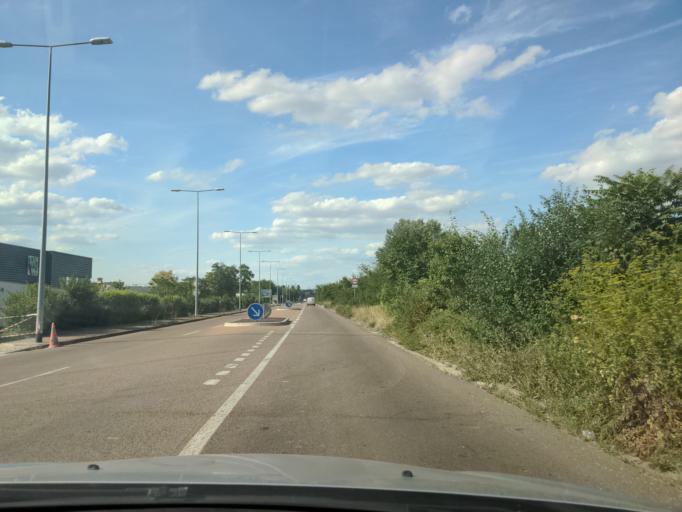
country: FR
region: Bourgogne
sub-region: Departement de la Cote-d'Or
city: Saint-Apollinaire
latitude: 47.3408
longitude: 5.0630
